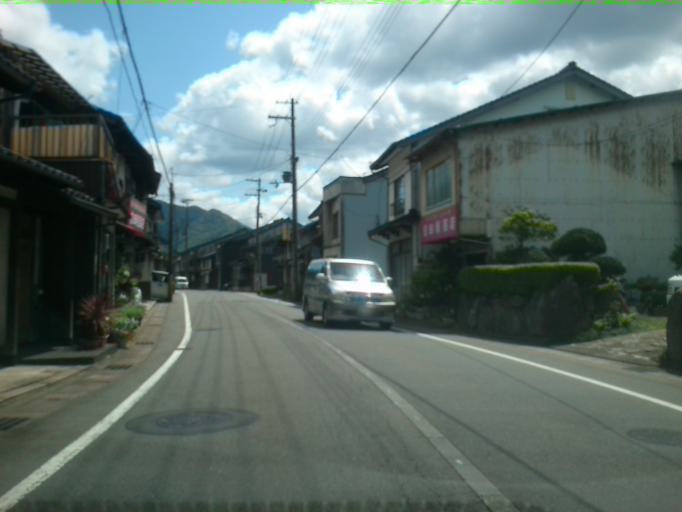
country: JP
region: Hyogo
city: Toyooka
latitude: 35.4664
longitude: 134.8711
